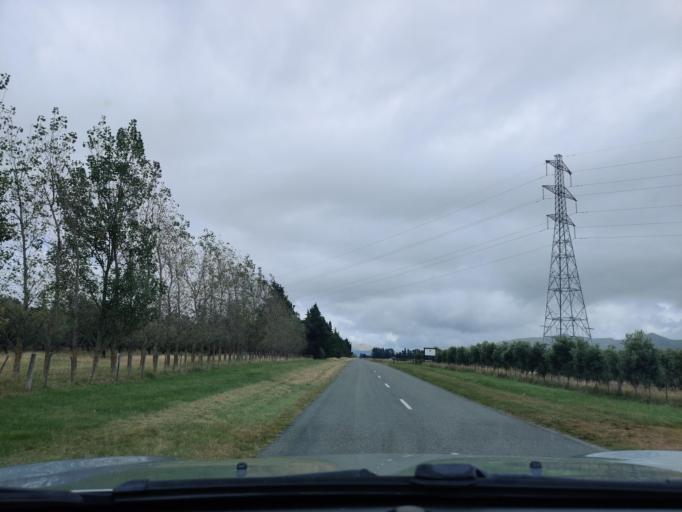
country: NZ
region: Canterbury
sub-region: Hurunui District
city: Amberley
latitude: -43.0763
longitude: 172.7054
